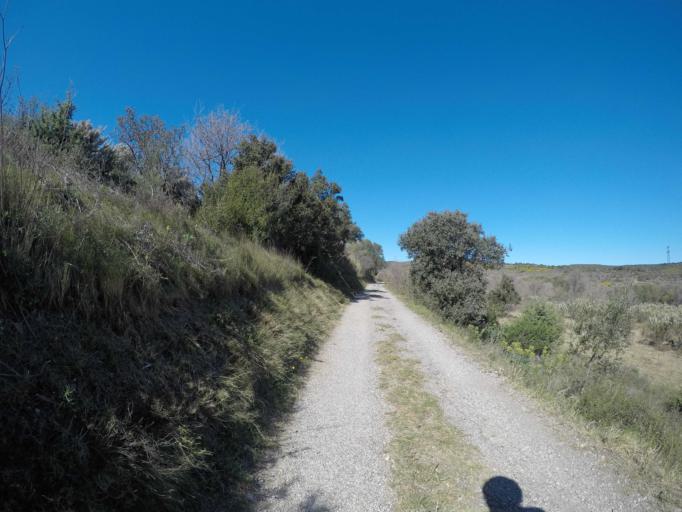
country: FR
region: Languedoc-Roussillon
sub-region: Departement des Pyrenees-Orientales
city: Millas
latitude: 42.7077
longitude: 2.6687
